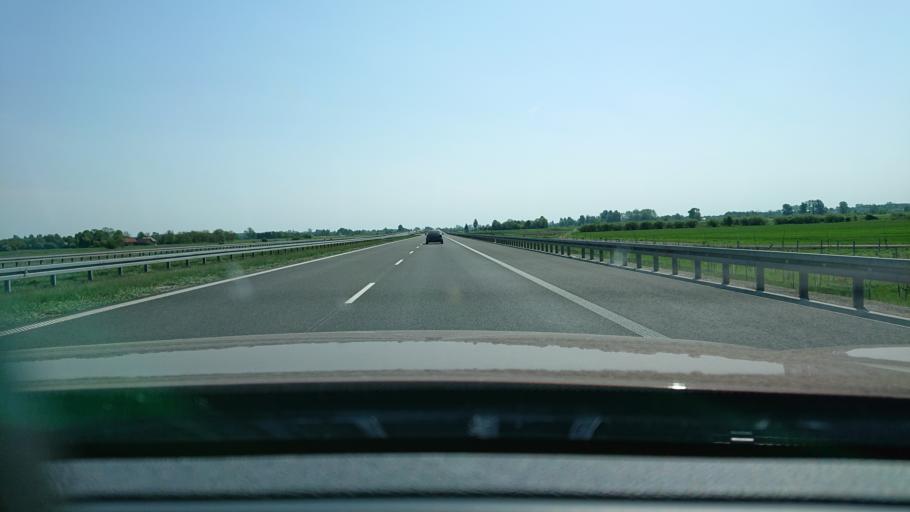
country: PL
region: Subcarpathian Voivodeship
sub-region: Powiat lancucki
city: Bialobrzegi
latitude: 50.1140
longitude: 22.3512
